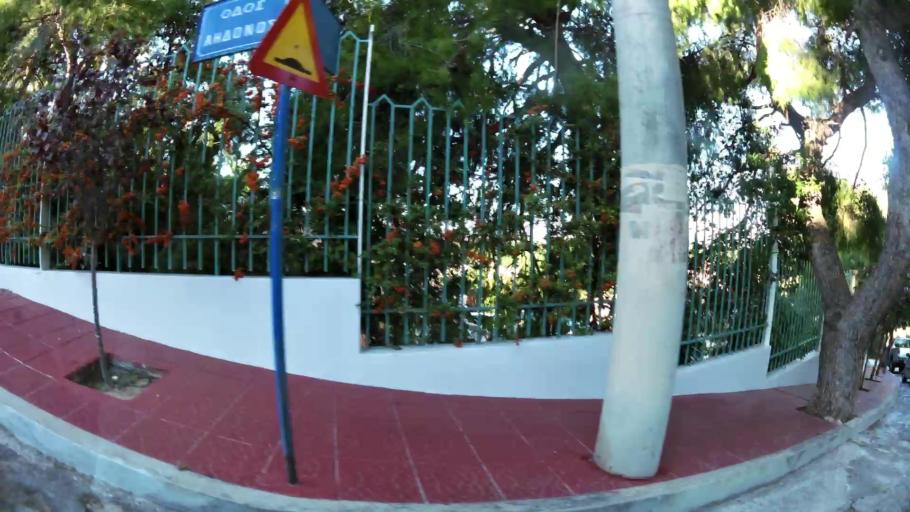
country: GR
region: Attica
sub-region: Nomarchia Anatolikis Attikis
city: Drosia
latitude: 38.1092
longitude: 23.8529
